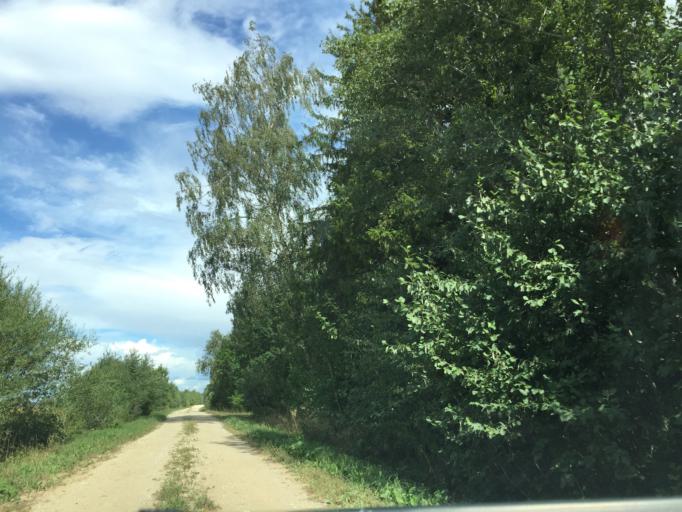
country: LT
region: Siauliu apskritis
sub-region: Joniskis
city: Joniskis
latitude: 56.3015
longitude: 23.6466
